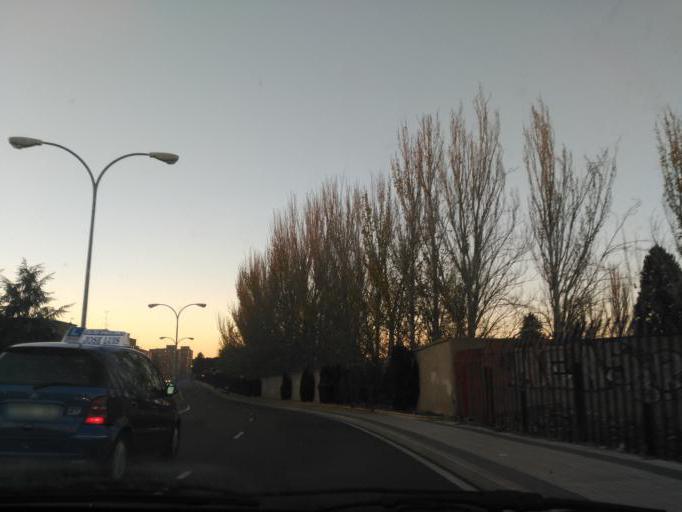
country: ES
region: Castille and Leon
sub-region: Provincia de Salamanca
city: Carbajosa de la Sagrada
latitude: 40.9482
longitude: -5.6566
